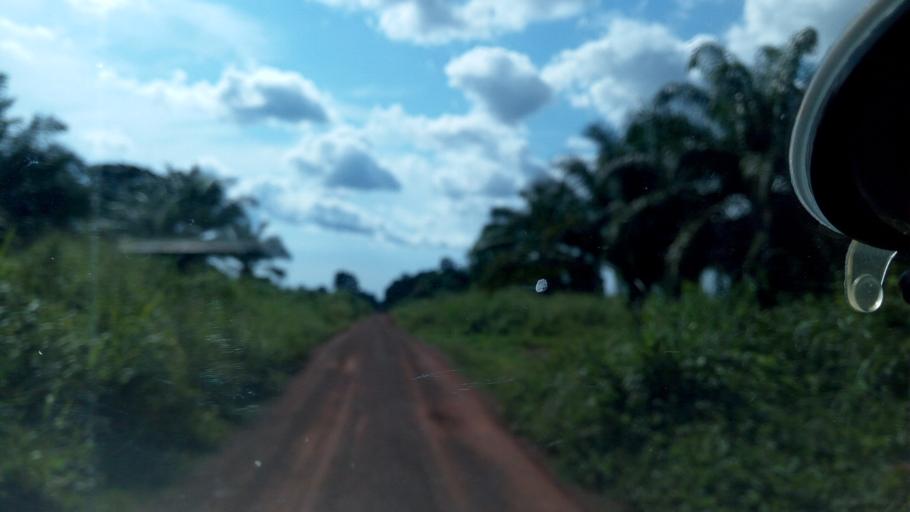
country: CD
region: Equateur
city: Libenge
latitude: 3.7394
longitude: 18.7516
